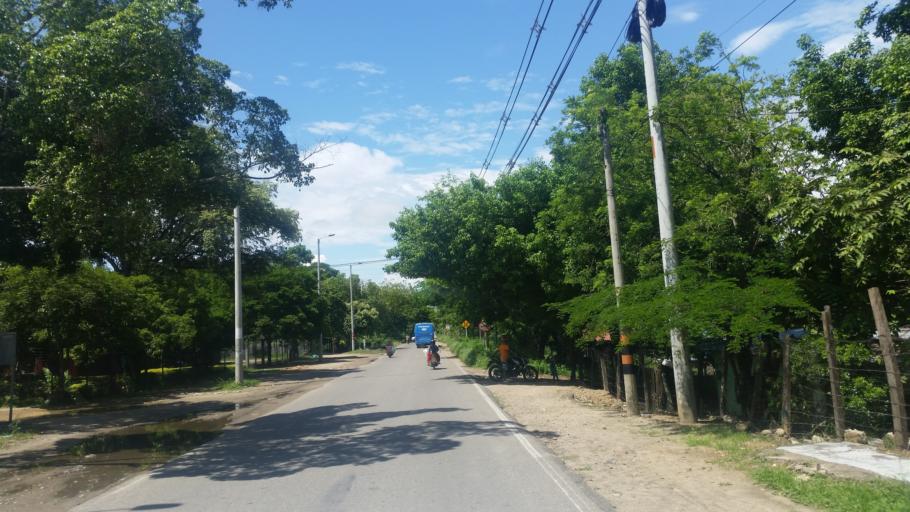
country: CO
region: Huila
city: Neiva
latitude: 2.9842
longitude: -75.2797
